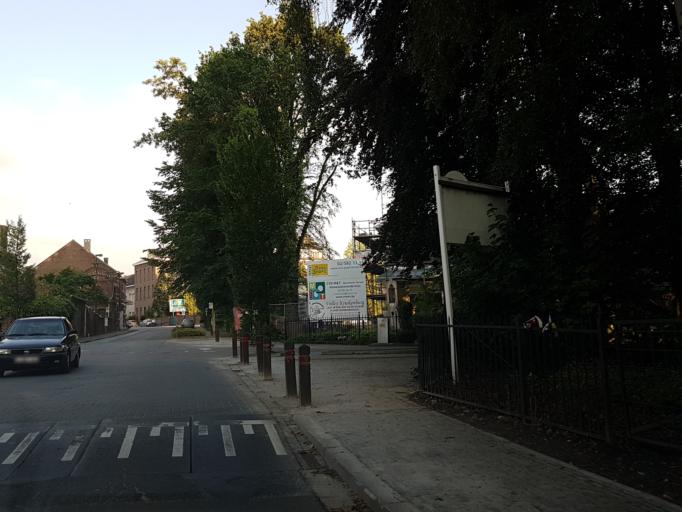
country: BE
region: Flanders
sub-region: Provincie Vlaams-Brabant
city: Ternat
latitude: 50.8716
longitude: 4.1726
